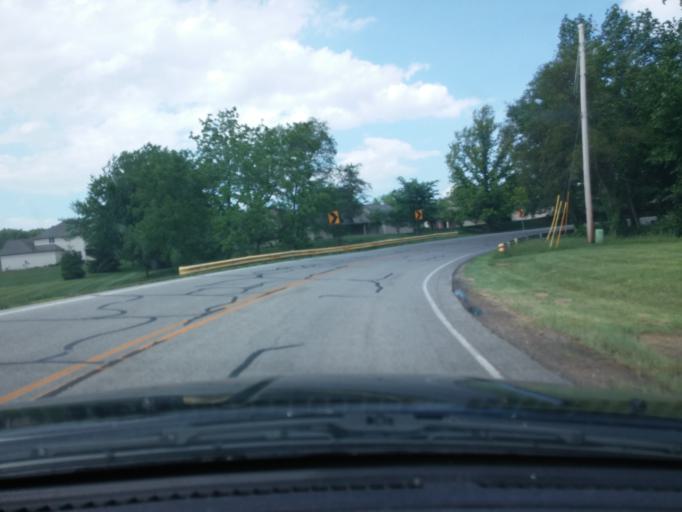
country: US
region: Indiana
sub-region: Tippecanoe County
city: West Lafayette
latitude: 40.4701
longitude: -86.8995
